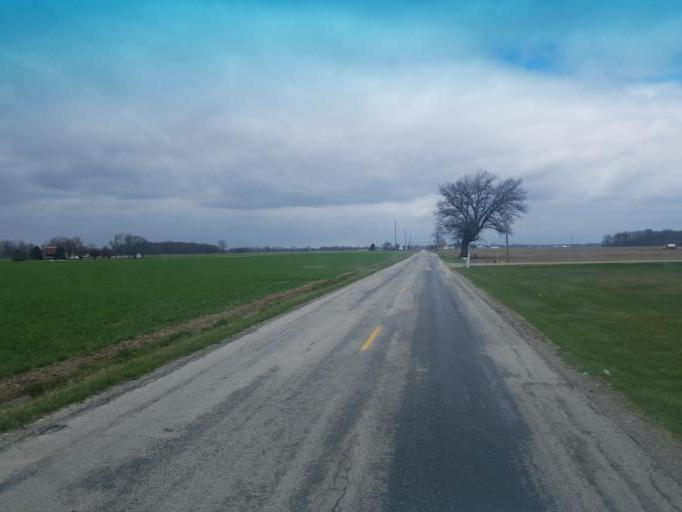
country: US
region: Ohio
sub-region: Marion County
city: Prospect
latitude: 40.4491
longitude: -83.1574
